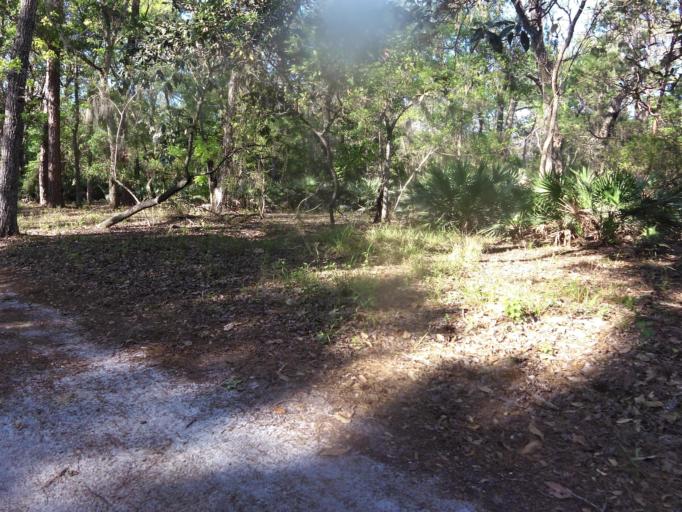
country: US
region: Florida
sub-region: Saint Johns County
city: Villano Beach
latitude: 30.0168
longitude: -81.3334
